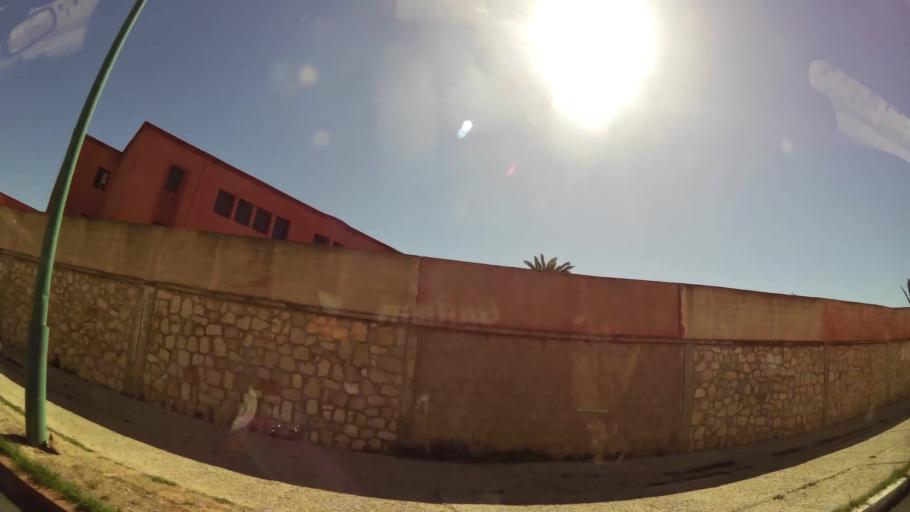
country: MA
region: Meknes-Tafilalet
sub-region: Meknes
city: Meknes
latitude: 33.9065
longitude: -5.5465
